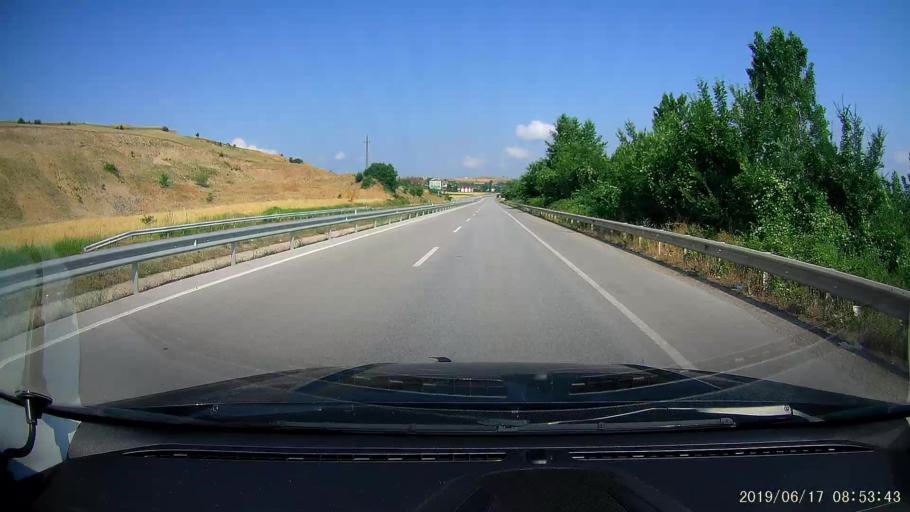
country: TR
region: Tokat
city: Erbaa
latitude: 40.7123
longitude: 36.4756
